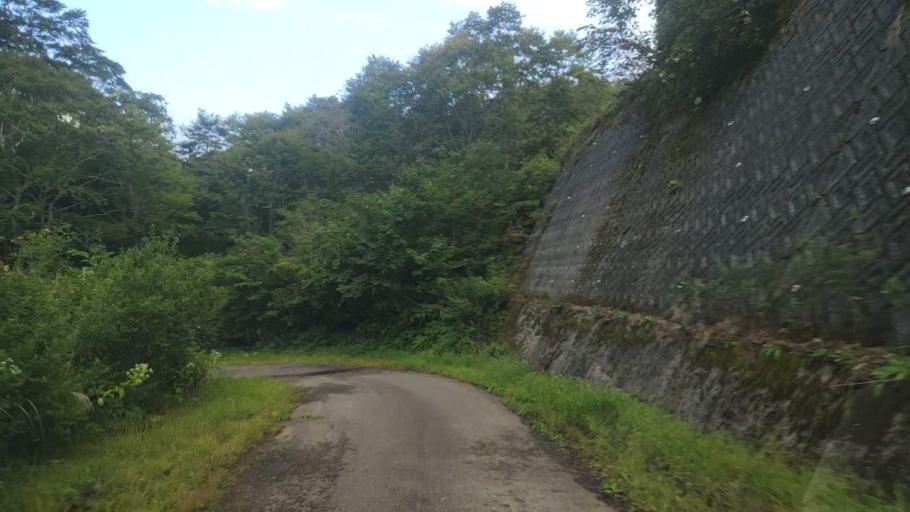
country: JP
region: Toyama
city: Yatsuomachi-higashikumisaka
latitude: 36.3487
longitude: 137.0648
